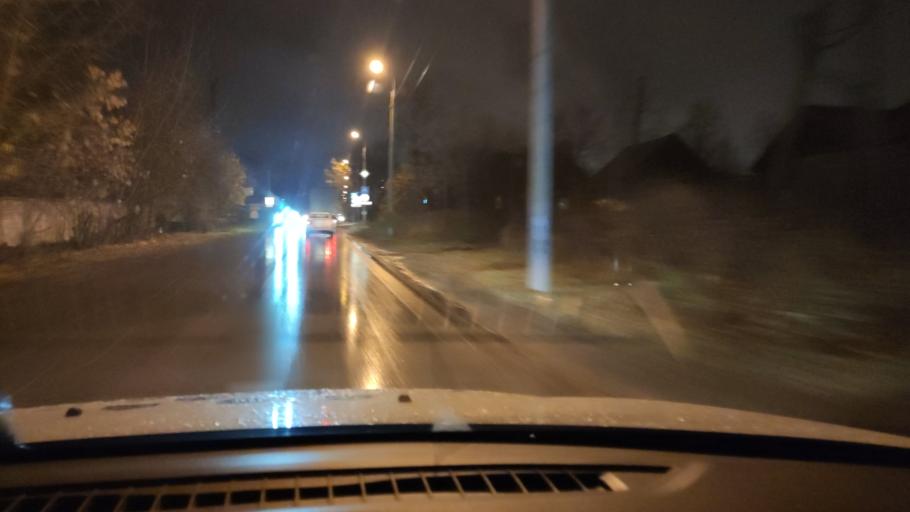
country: RU
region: Perm
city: Perm
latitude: 57.9929
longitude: 56.3078
